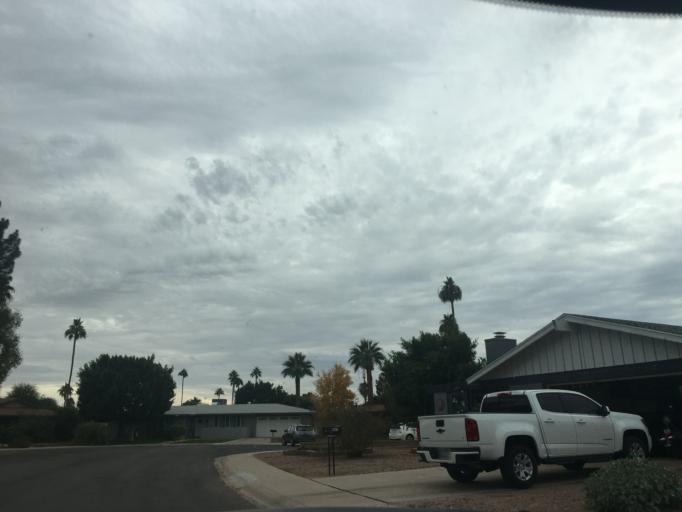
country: US
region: Arizona
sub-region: Maricopa County
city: Tempe
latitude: 33.3829
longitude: -111.9054
